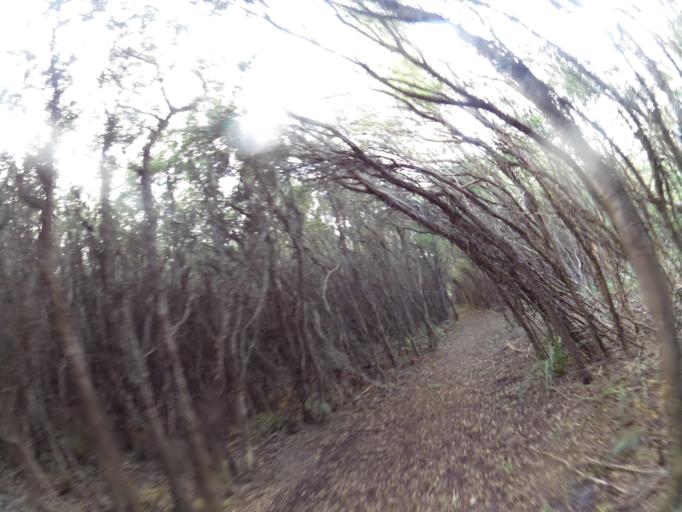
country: AU
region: Victoria
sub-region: Bass Coast
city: North Wonthaggi
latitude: -38.6426
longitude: 145.5641
